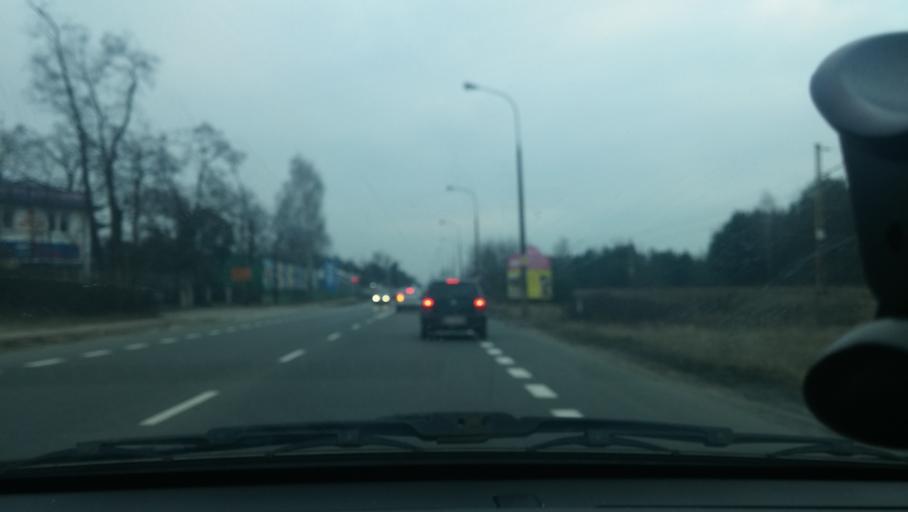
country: PL
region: Masovian Voivodeship
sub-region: Warszawa
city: Wawer
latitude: 52.1952
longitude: 21.1782
